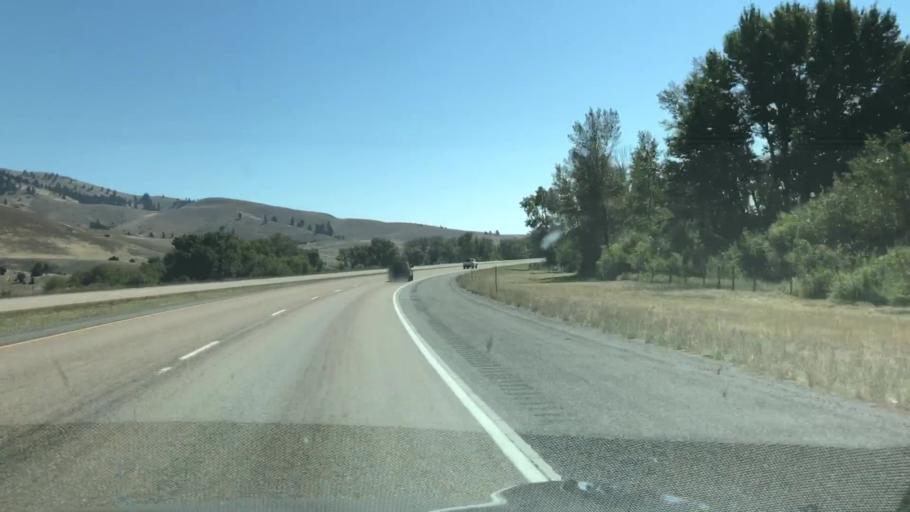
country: US
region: Montana
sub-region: Granite County
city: Philipsburg
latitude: 46.6977
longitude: -113.2087
